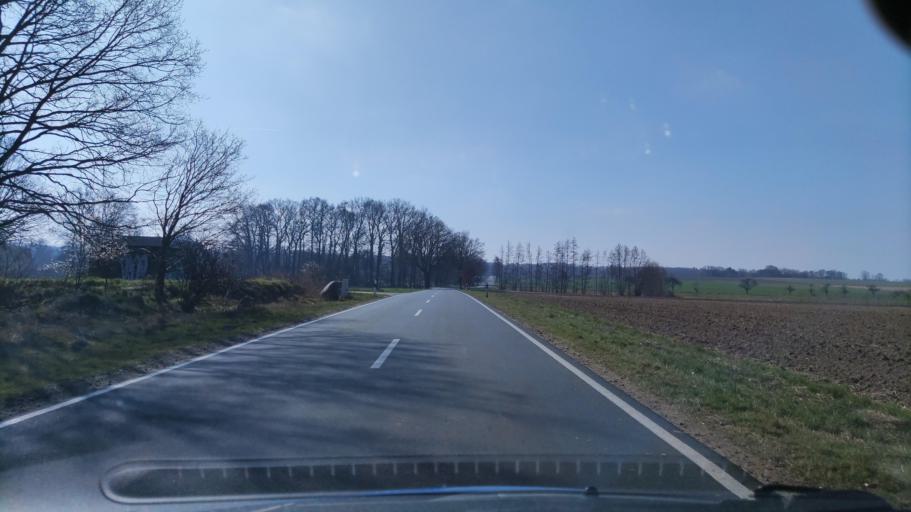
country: DE
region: Lower Saxony
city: Kusten
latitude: 52.9720
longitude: 11.0646
